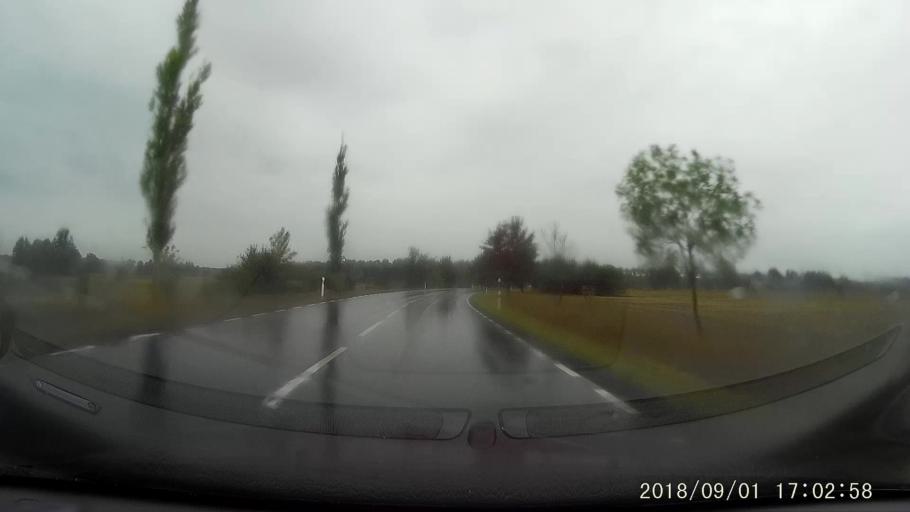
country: PL
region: Lubusz
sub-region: Powiat zielonogorski
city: Swidnica
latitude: 51.8788
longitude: 15.3764
